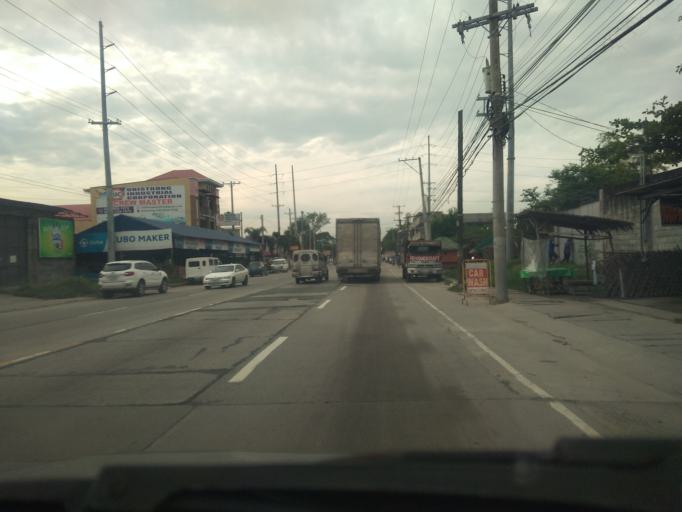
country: PH
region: Central Luzon
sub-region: Province of Pampanga
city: San Fernando
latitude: 15.0259
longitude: 120.6975
